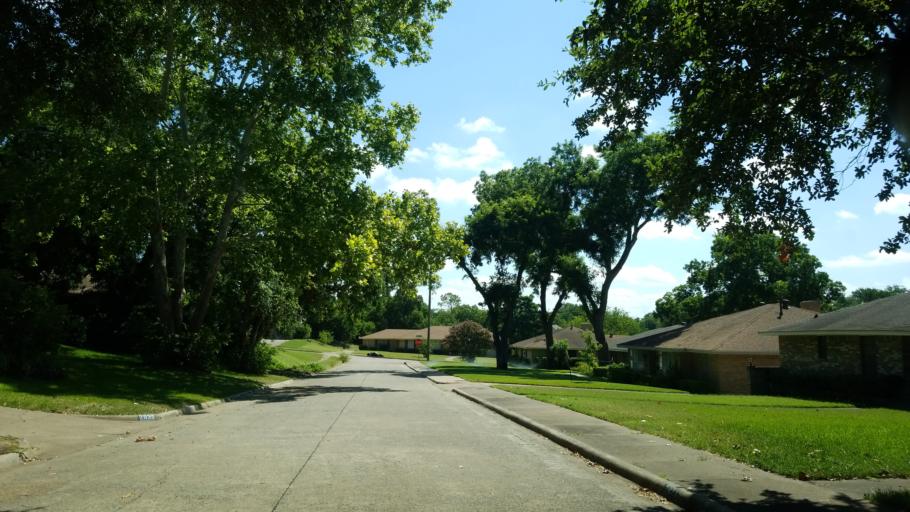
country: US
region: Texas
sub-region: Dallas County
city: Dallas
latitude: 32.7267
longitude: -96.7934
